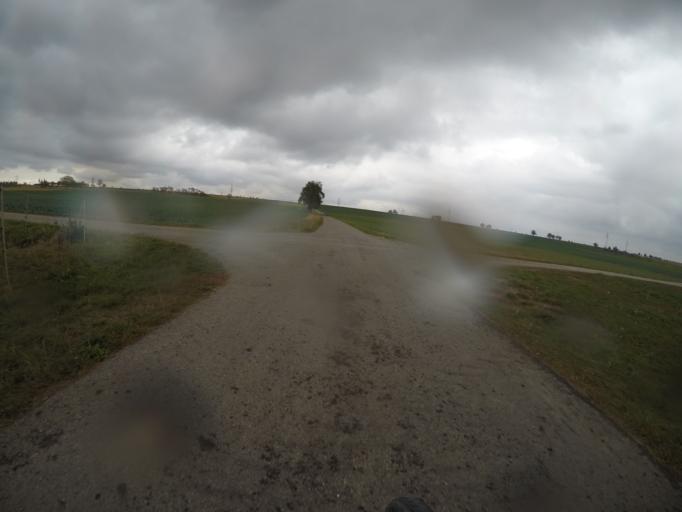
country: DE
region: Baden-Wuerttemberg
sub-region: Regierungsbezirk Stuttgart
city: Herrenberg
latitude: 48.6119
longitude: 8.8575
